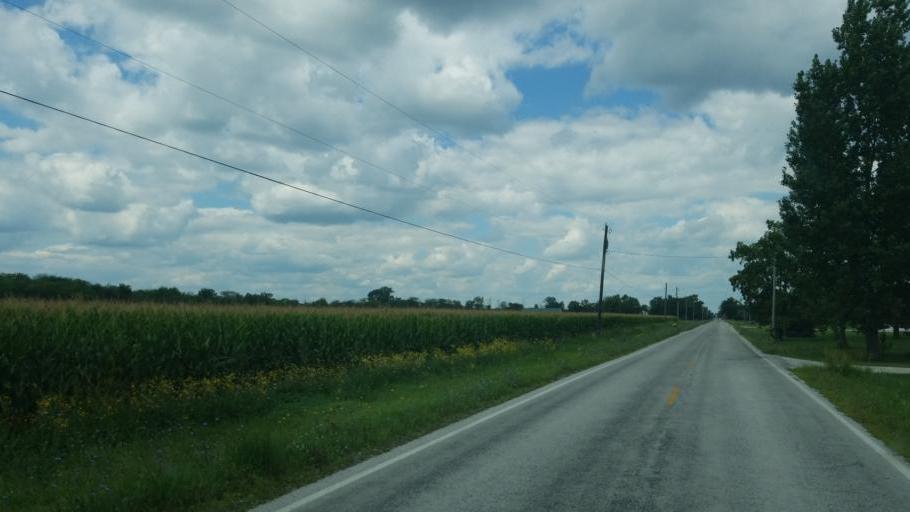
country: US
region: Ohio
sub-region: Ottawa County
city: Elmore
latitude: 41.5287
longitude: -83.2801
